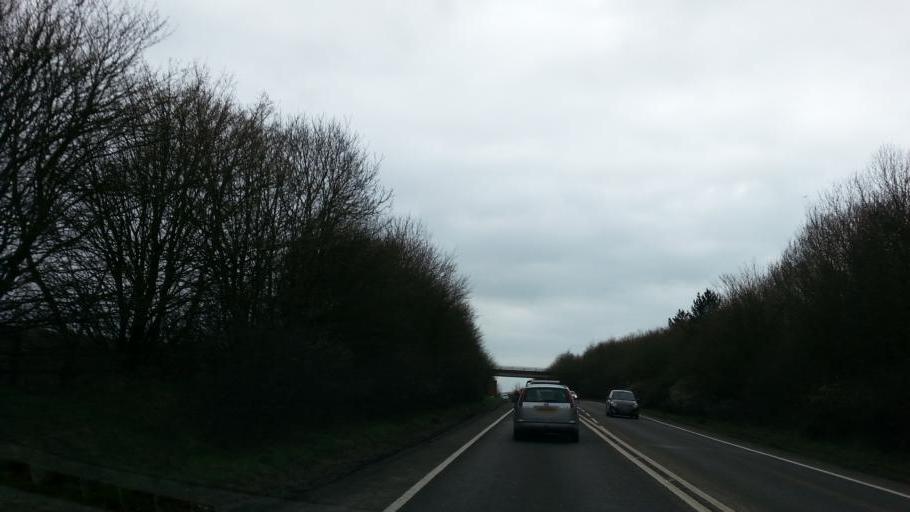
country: GB
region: England
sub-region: Devon
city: Appledore
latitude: 51.0324
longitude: -4.1786
